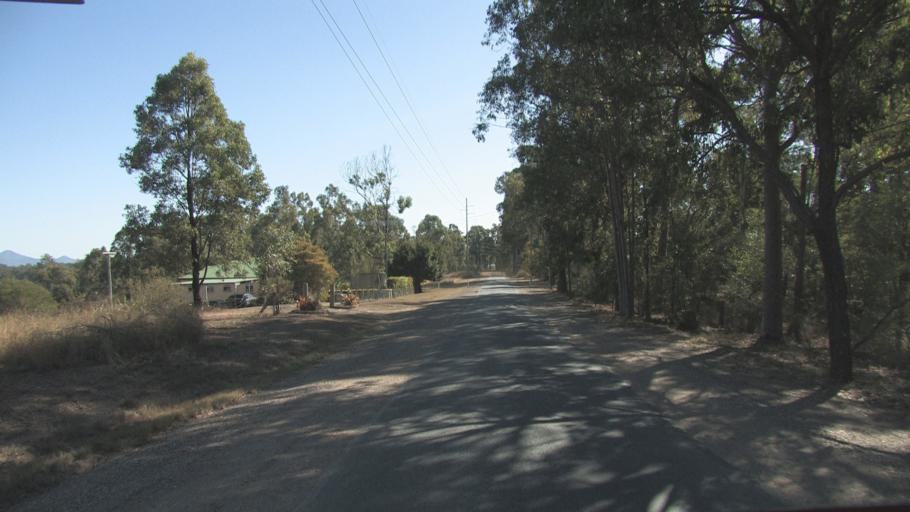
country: AU
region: Queensland
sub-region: Logan
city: Cedar Vale
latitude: -27.8916
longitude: 153.0178
